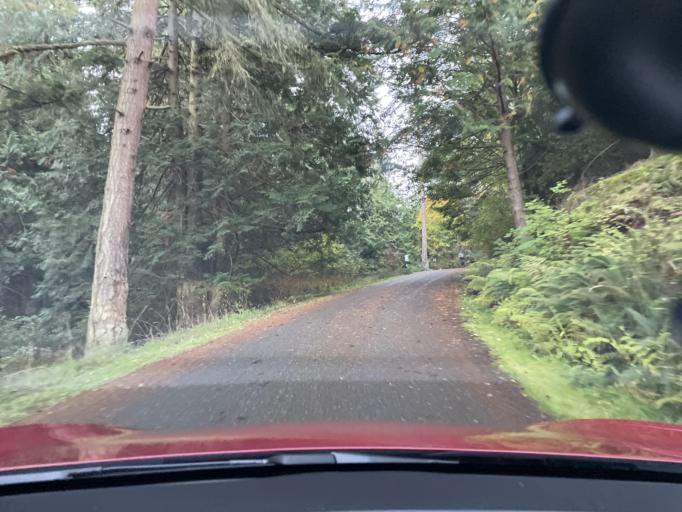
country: US
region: Washington
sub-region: San Juan County
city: Friday Harbor
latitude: 48.6189
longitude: -123.1414
